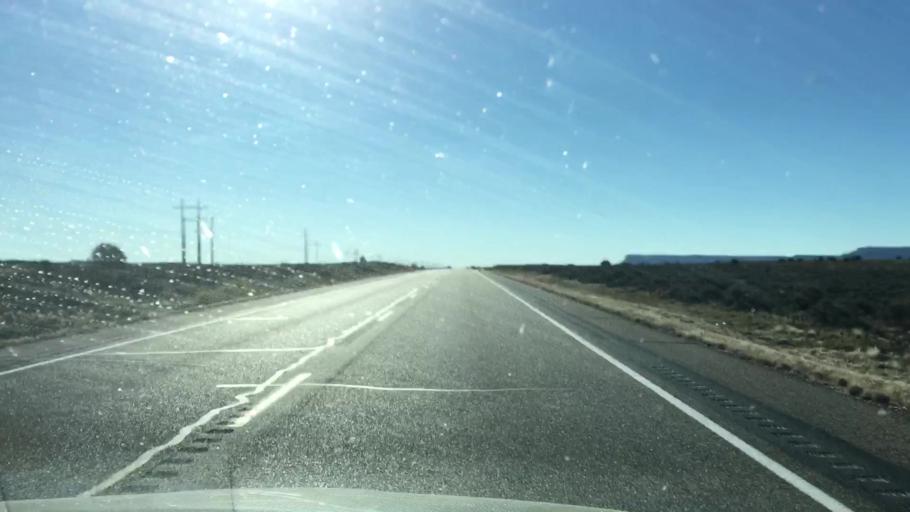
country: US
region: Utah
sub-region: Kane County
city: Kanab
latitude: 37.1745
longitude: -112.0176
